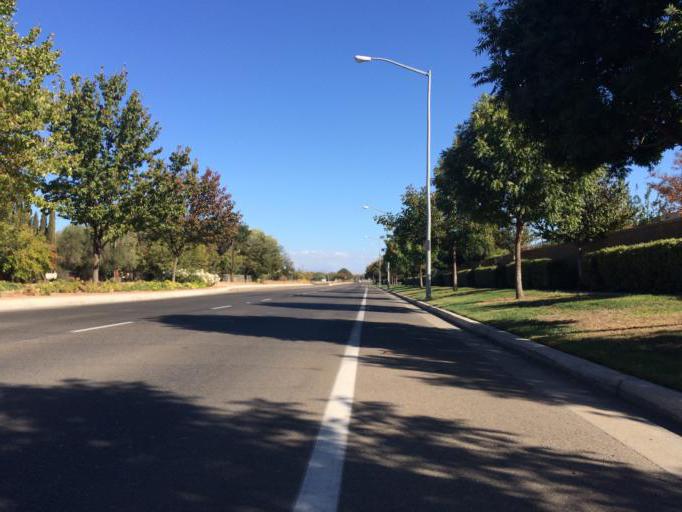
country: US
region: California
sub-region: Fresno County
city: Clovis
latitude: 36.8666
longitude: -119.7082
